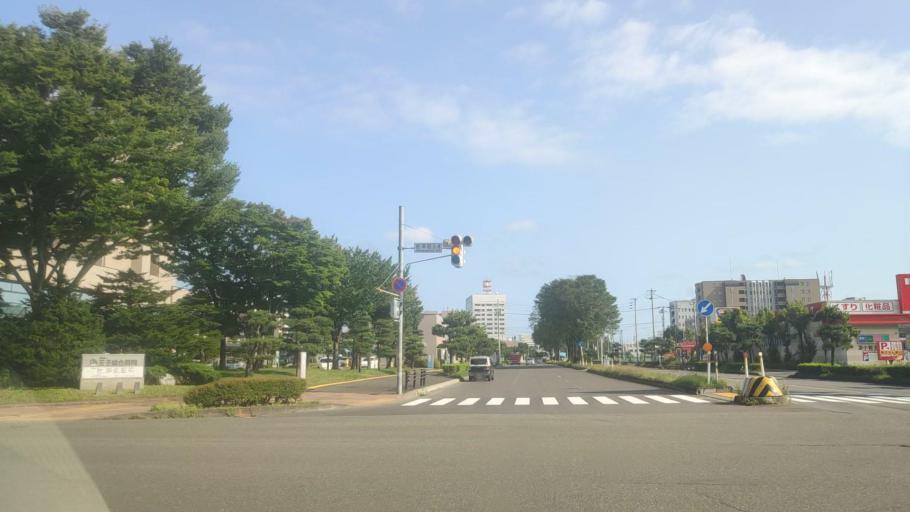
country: JP
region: Hokkaido
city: Tomakomai
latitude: 42.6387
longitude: 141.6021
